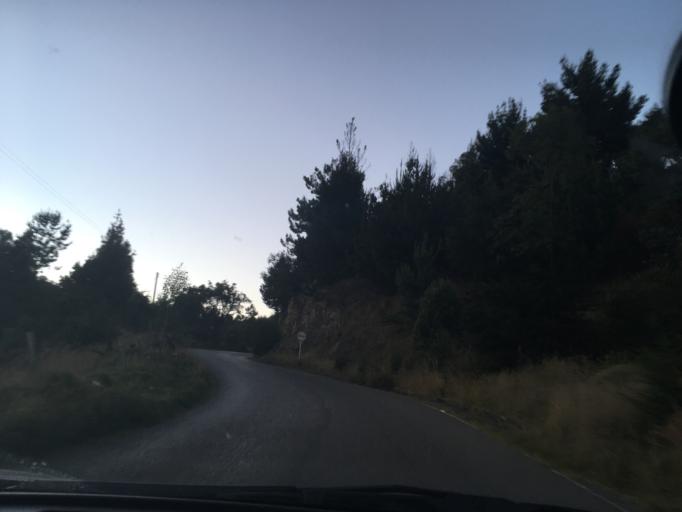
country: CO
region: Boyaca
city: Aquitania
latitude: 5.6108
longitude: -72.9113
